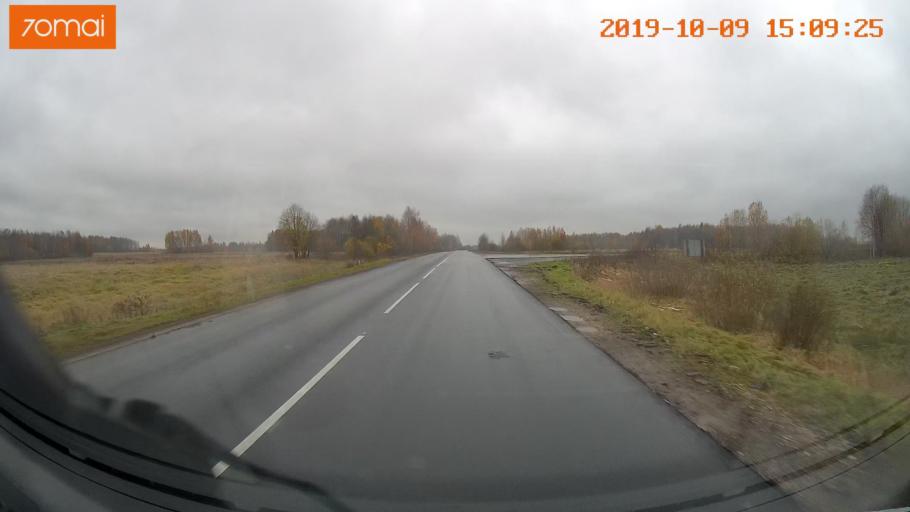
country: RU
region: Kostroma
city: Susanino
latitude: 58.1919
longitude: 41.6503
